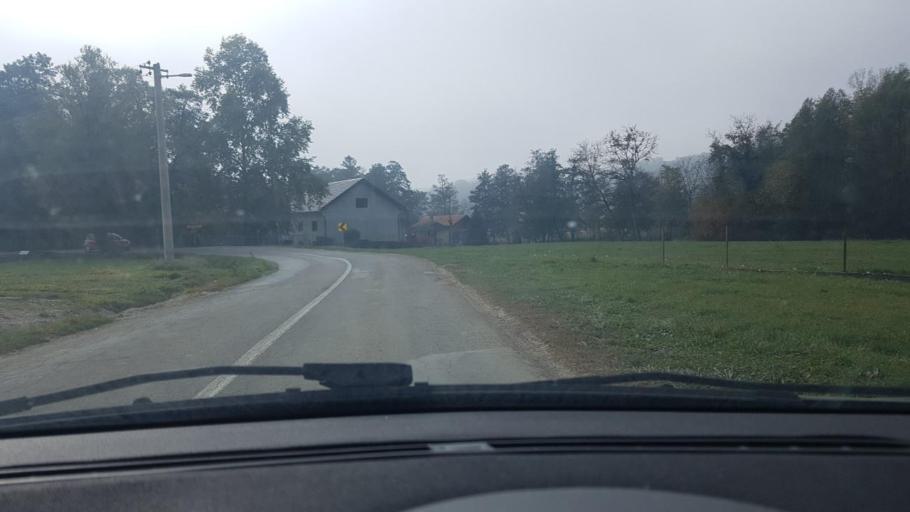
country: HR
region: Krapinsko-Zagorska
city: Zlatar
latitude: 46.1352
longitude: 16.0702
